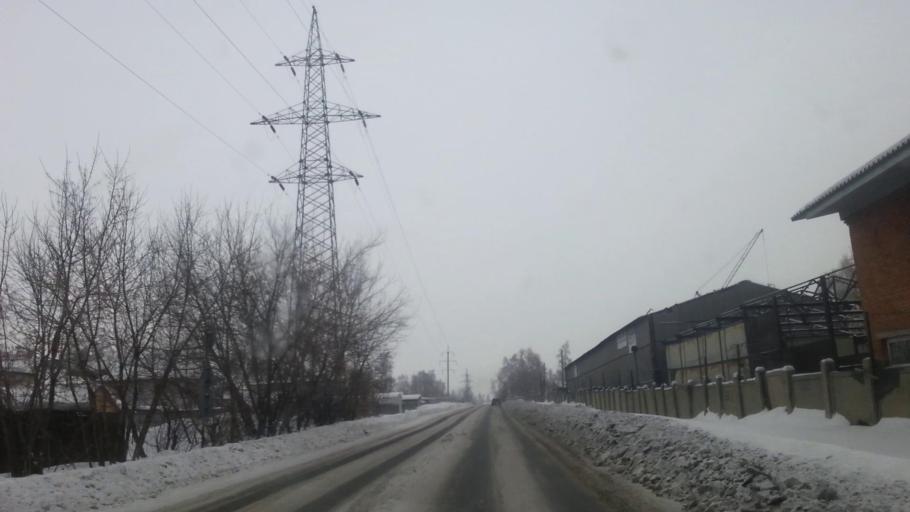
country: RU
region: Altai Krai
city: Novosilikatnyy
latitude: 53.3115
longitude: 83.6189
